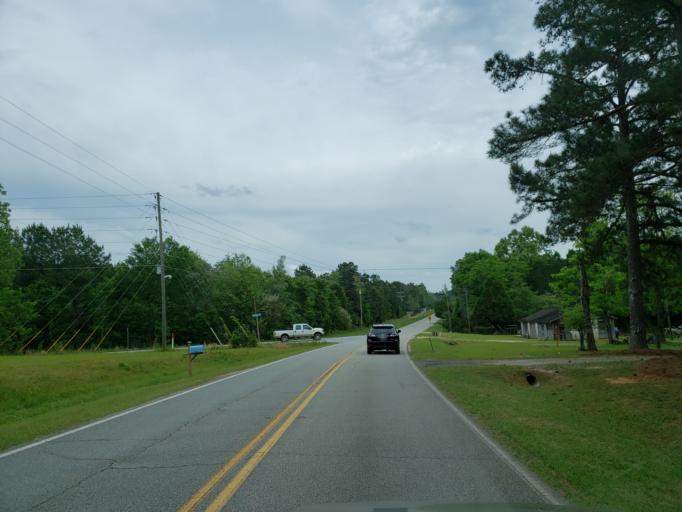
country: US
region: Georgia
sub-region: Bibb County
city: West Point
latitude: 32.8149
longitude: -83.8521
